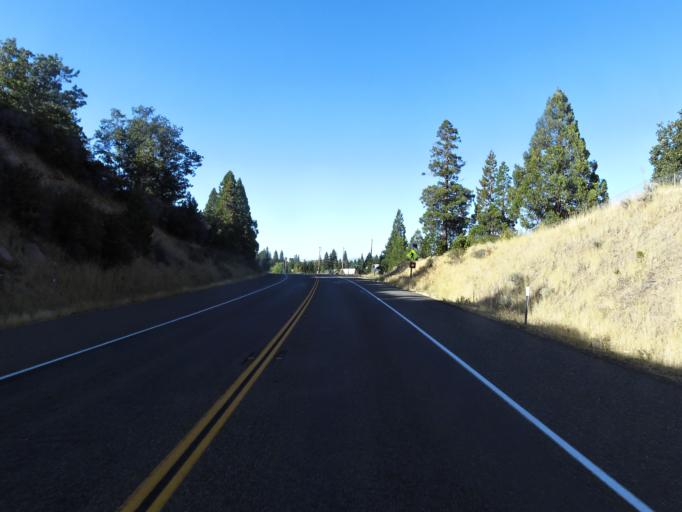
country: US
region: California
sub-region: Siskiyou County
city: Weed
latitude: 41.4344
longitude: -122.3872
